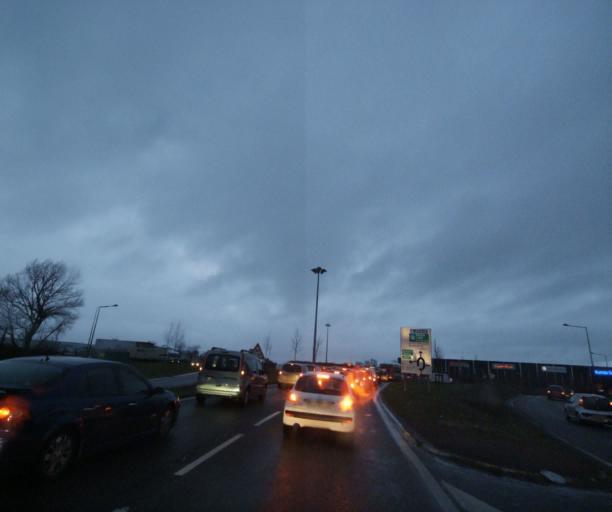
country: FR
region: Pays de la Loire
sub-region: Departement de la Sarthe
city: Coulaines
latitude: 48.0278
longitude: 0.1805
